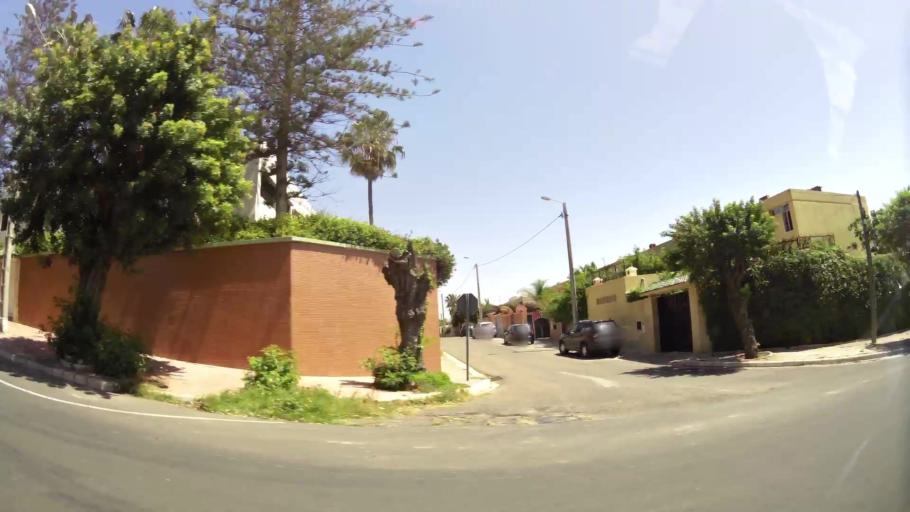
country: MA
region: Souss-Massa-Draa
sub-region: Agadir-Ida-ou-Tnan
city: Agadir
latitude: 30.4288
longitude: -9.6012
